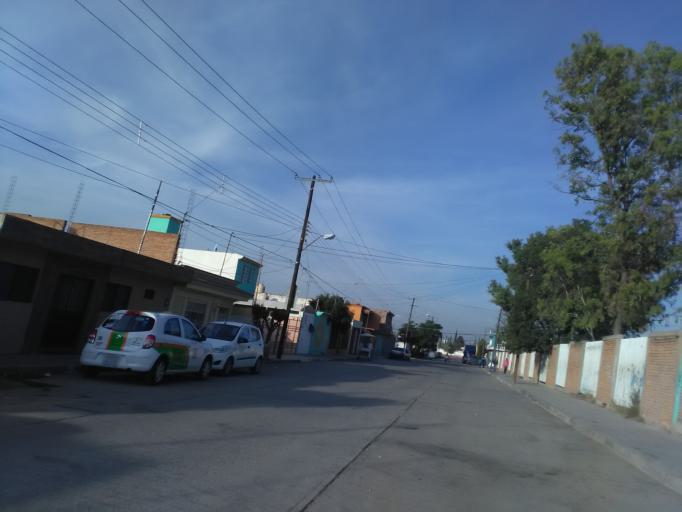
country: MX
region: Durango
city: Victoria de Durango
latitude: 24.0440
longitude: -104.6487
